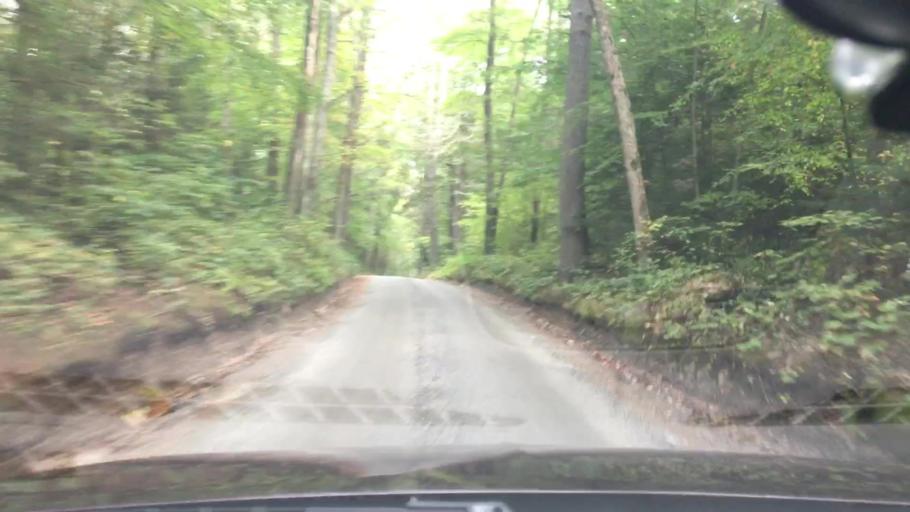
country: US
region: Connecticut
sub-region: Tolland County
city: Stafford
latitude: 41.9846
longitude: -72.3293
